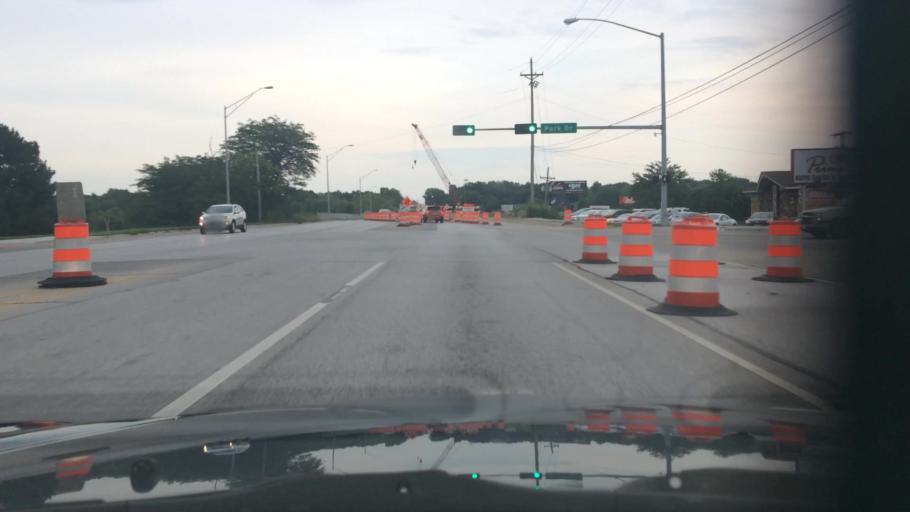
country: US
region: Nebraska
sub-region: Douglas County
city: Ralston
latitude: 41.2010
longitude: -96.0431
